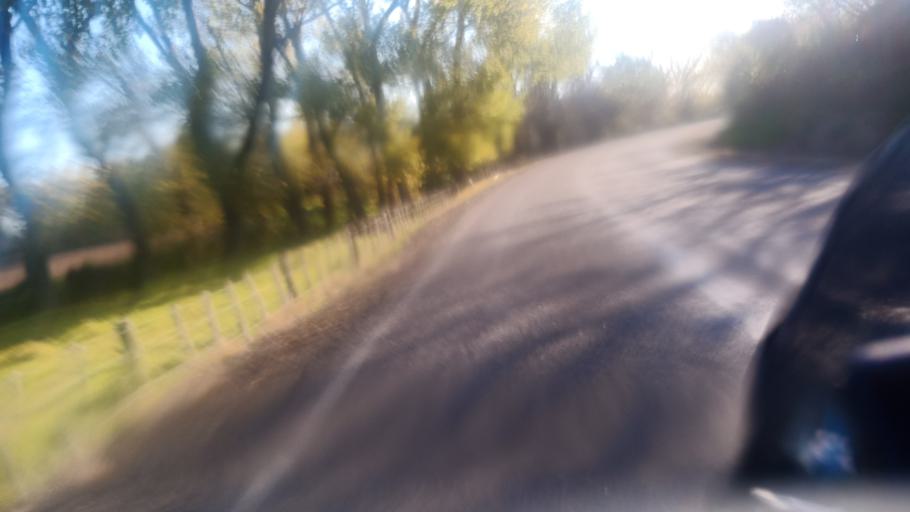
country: NZ
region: Hawke's Bay
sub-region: Wairoa District
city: Wairoa
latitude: -39.0482
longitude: 177.7599
